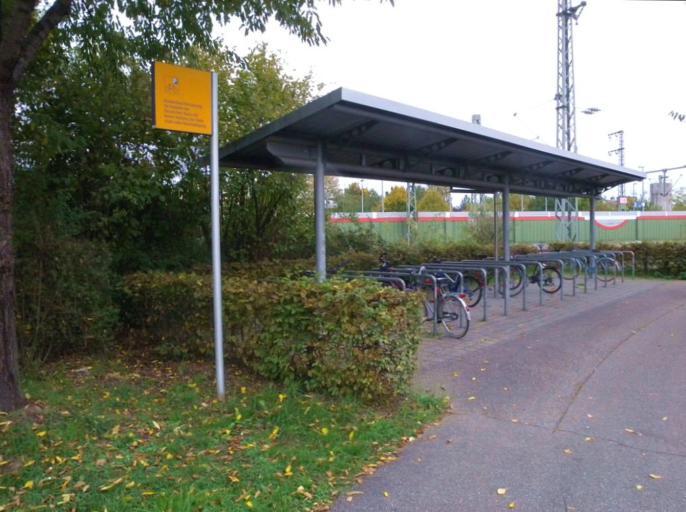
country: DE
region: Baden-Wuerttemberg
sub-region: Freiburg Region
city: Appenweier
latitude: 48.5415
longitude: 7.9727
